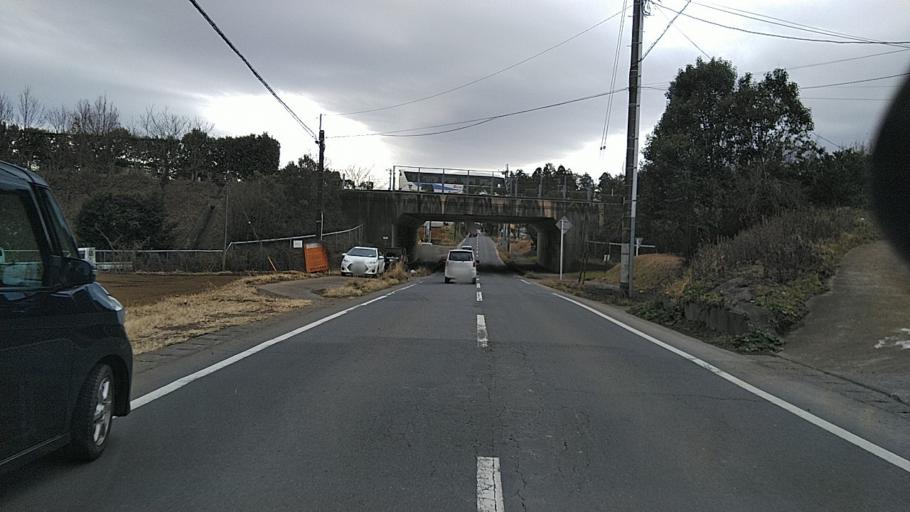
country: JP
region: Chiba
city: Sawara
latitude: 35.8397
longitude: 140.4552
